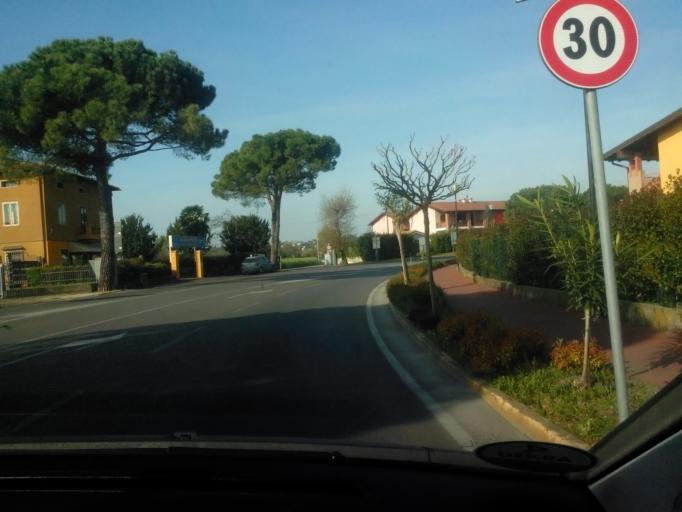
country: IT
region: Lombardy
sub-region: Provincia di Brescia
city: Manerba del Garda
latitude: 45.5478
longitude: 10.5400
